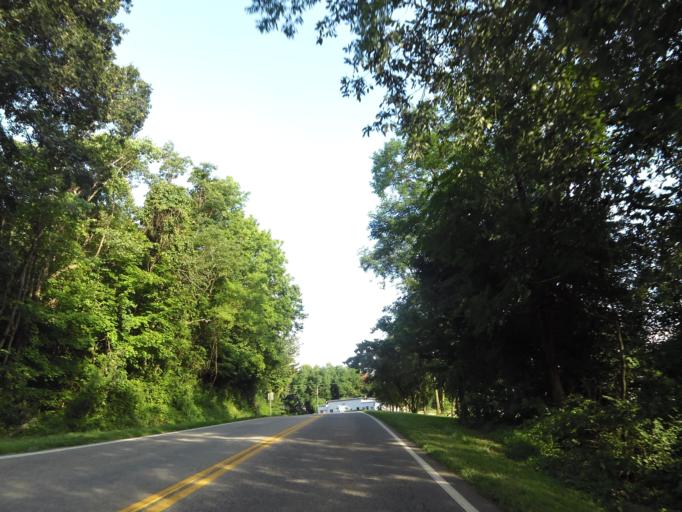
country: US
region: Tennessee
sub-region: Blount County
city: Louisville
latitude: 35.8195
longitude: -84.0336
